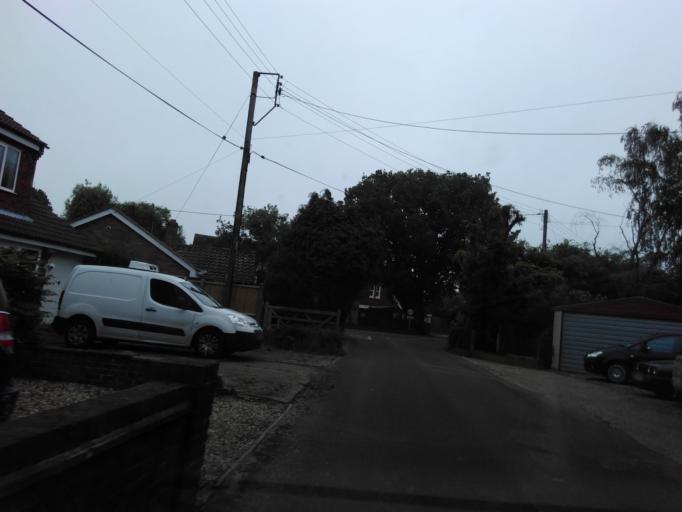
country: GB
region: England
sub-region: Kent
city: Chartham
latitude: 51.2713
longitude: 1.0130
